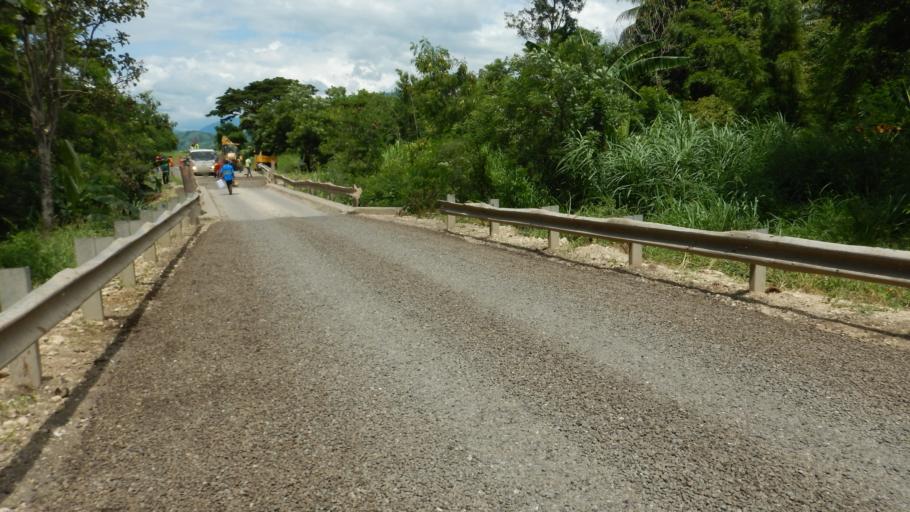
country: PG
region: Eastern Highlands
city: Kainantu
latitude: -5.9212
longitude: 145.8372
